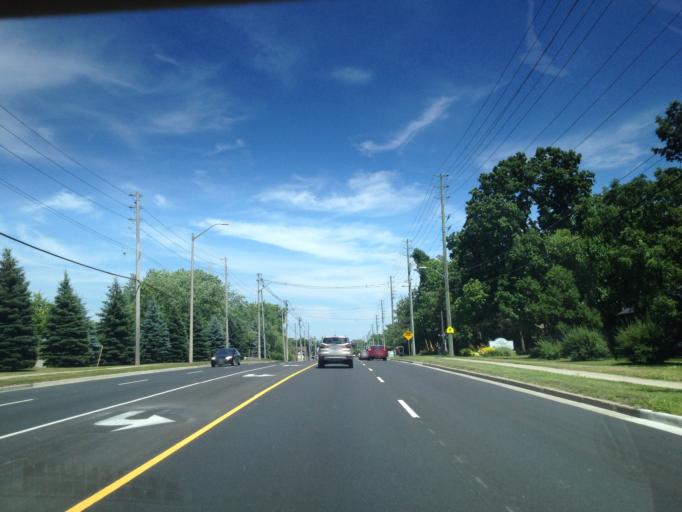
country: CA
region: Ontario
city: London
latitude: 42.9877
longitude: -81.2796
